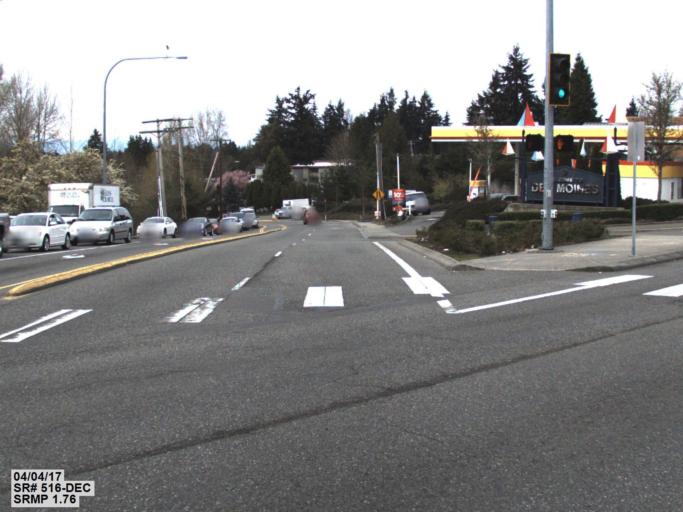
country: US
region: Washington
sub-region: King County
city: Des Moines
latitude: 47.3940
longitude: -122.2951
